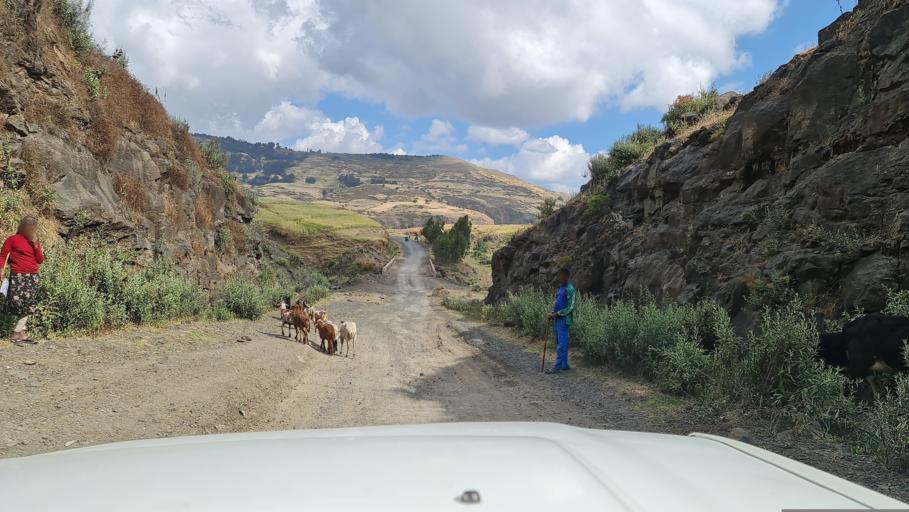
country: ET
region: Amhara
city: Debark'
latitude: 13.1328
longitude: 37.9279
